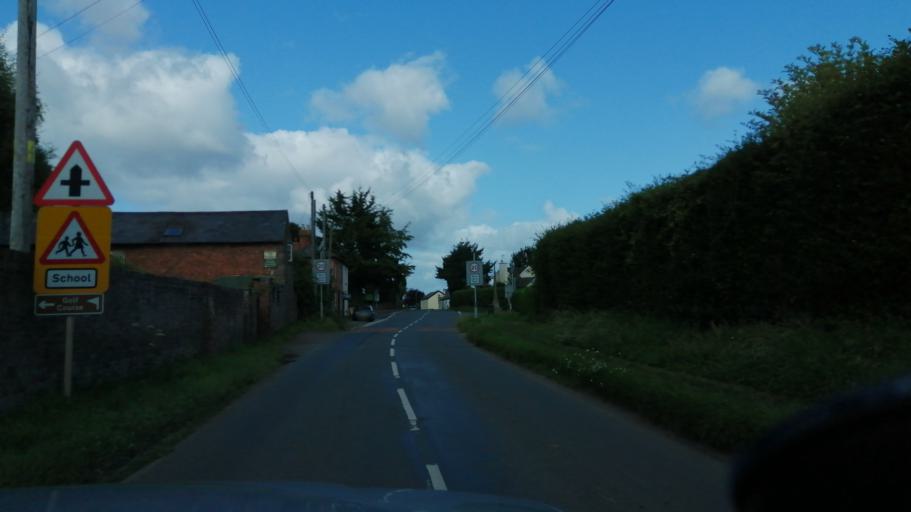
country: GB
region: England
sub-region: Herefordshire
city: Madley
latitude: 52.0442
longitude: -2.8459
